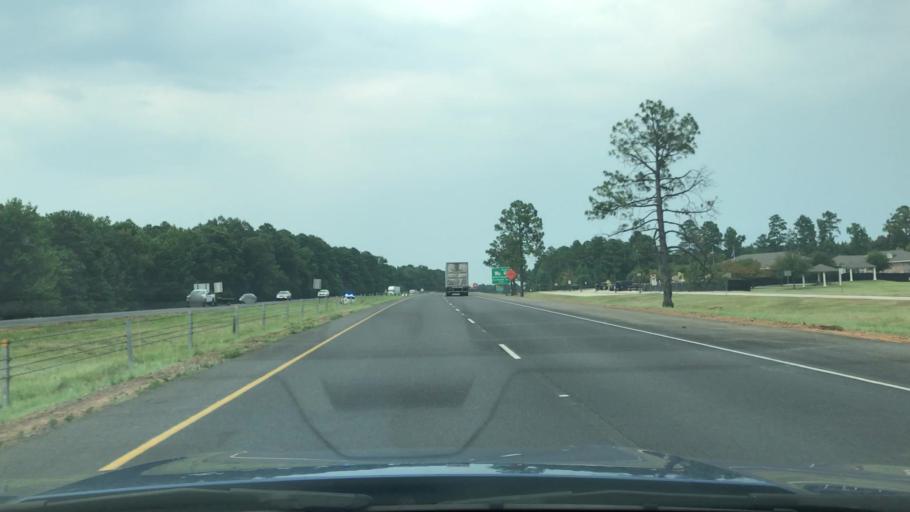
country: US
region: Louisiana
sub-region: Caddo Parish
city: Greenwood
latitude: 32.4516
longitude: -94.0036
